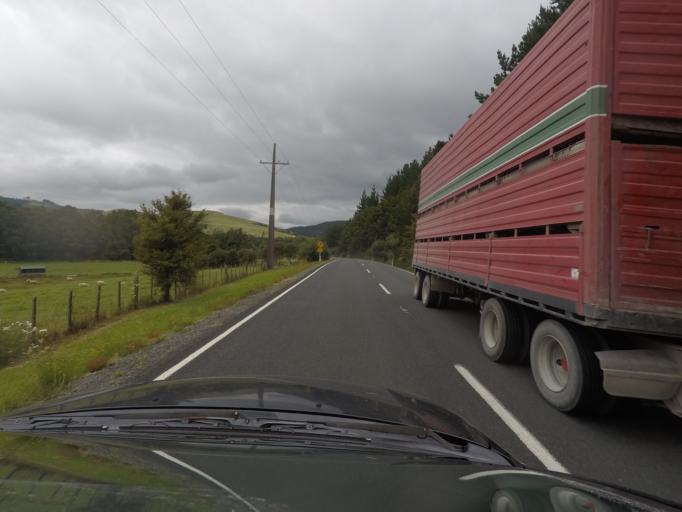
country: NZ
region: Auckland
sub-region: Auckland
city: Wellsford
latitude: -36.2889
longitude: 174.6136
